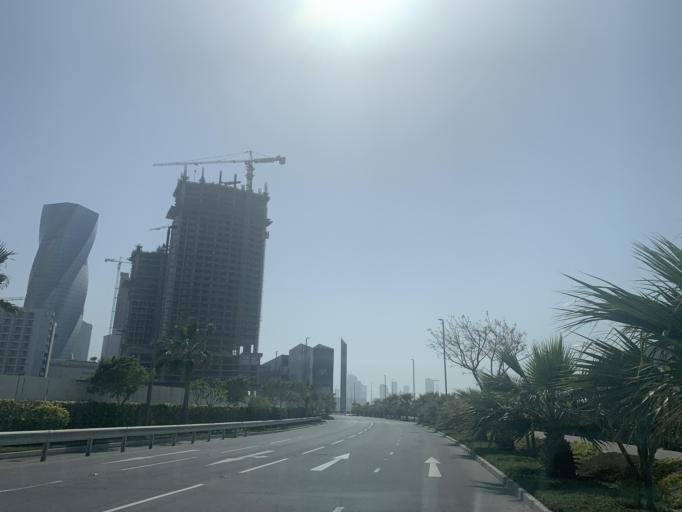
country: BH
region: Muharraq
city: Al Muharraq
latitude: 26.2514
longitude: 50.5794
